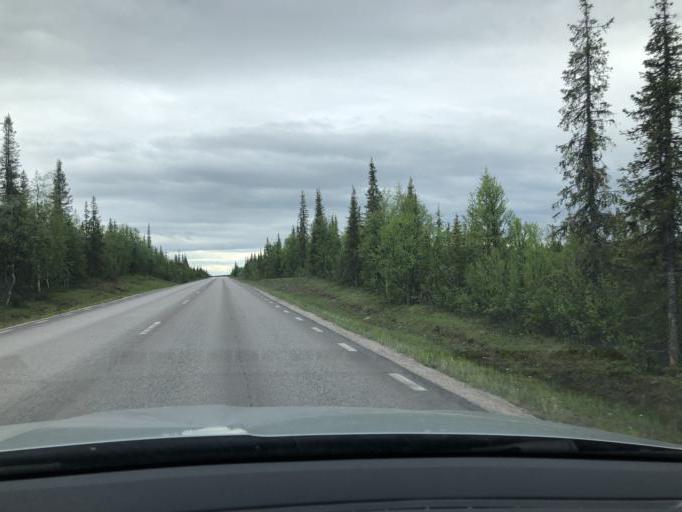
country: SE
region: Norrbotten
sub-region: Kiruna Kommun
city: Kiruna
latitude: 67.7204
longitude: 20.7204
